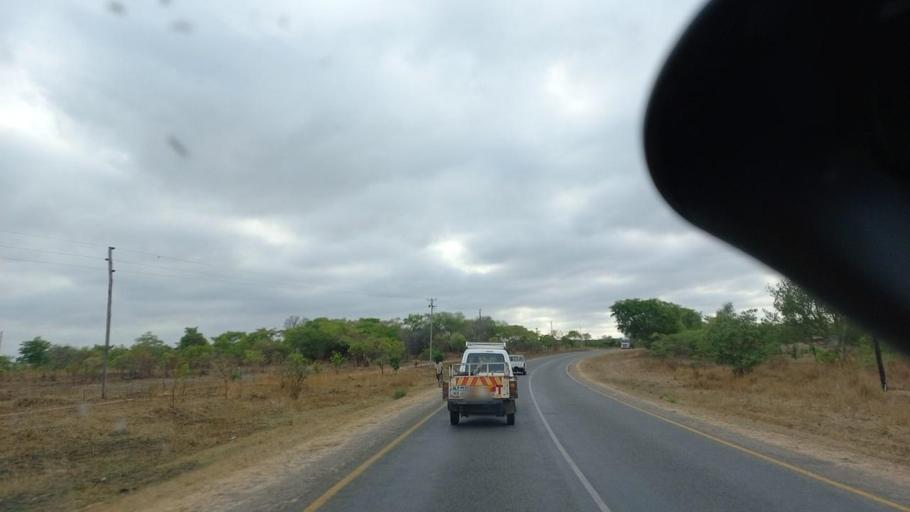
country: ZM
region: Lusaka
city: Chongwe
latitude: -15.2793
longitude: 28.7346
